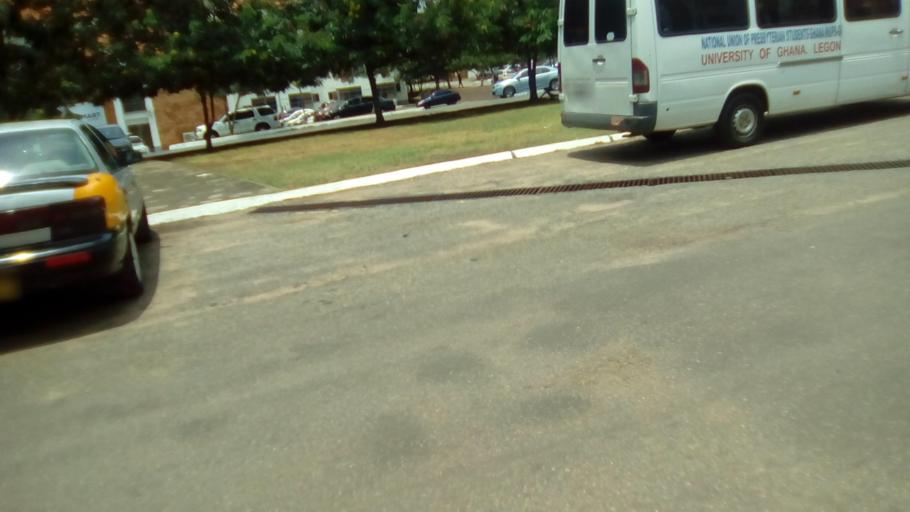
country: GH
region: Greater Accra
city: Medina Estates
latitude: 5.6567
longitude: -0.1818
